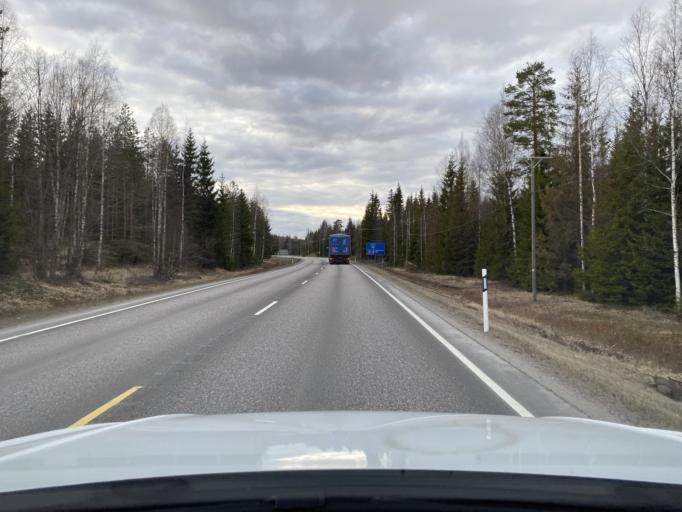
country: FI
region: Uusimaa
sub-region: Helsinki
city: Kaerkoelae
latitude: 60.8250
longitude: 24.0239
